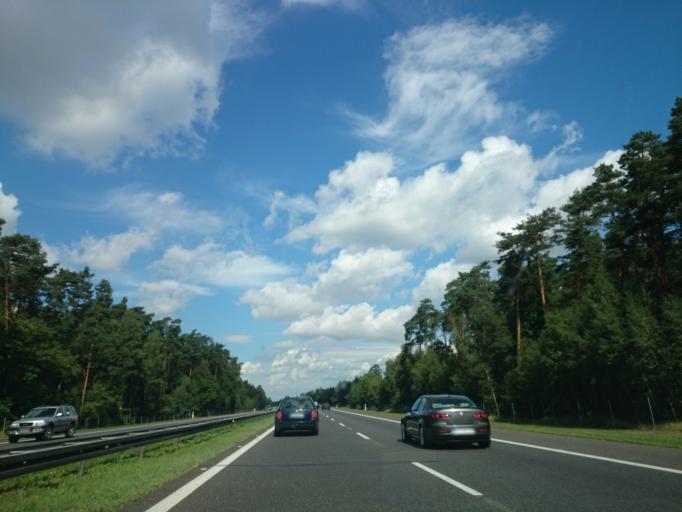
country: PL
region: Opole Voivodeship
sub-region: Powiat brzeski
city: Lewin Brzeski
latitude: 50.6990
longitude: 17.6211
